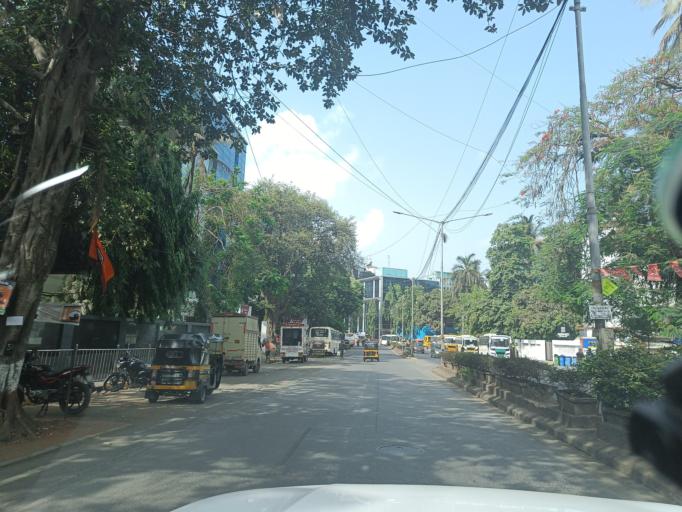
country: IN
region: Maharashtra
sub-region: Mumbai Suburban
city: Powai
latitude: 19.1229
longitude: 72.8713
